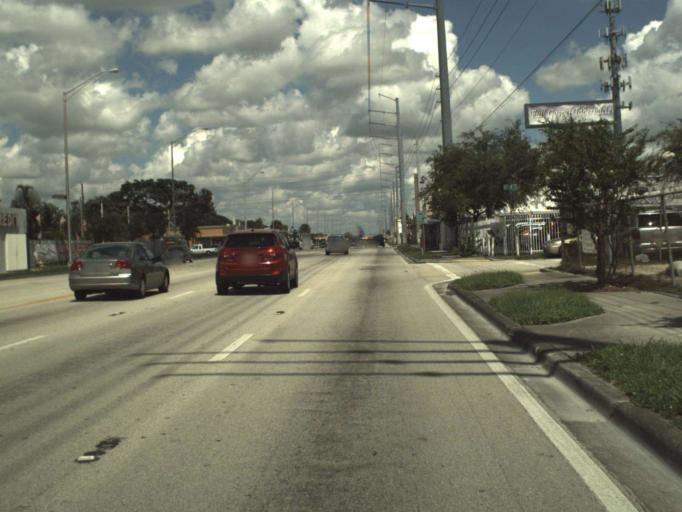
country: US
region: Florida
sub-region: Miami-Dade County
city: Pinewood
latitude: 25.8639
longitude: -80.2096
